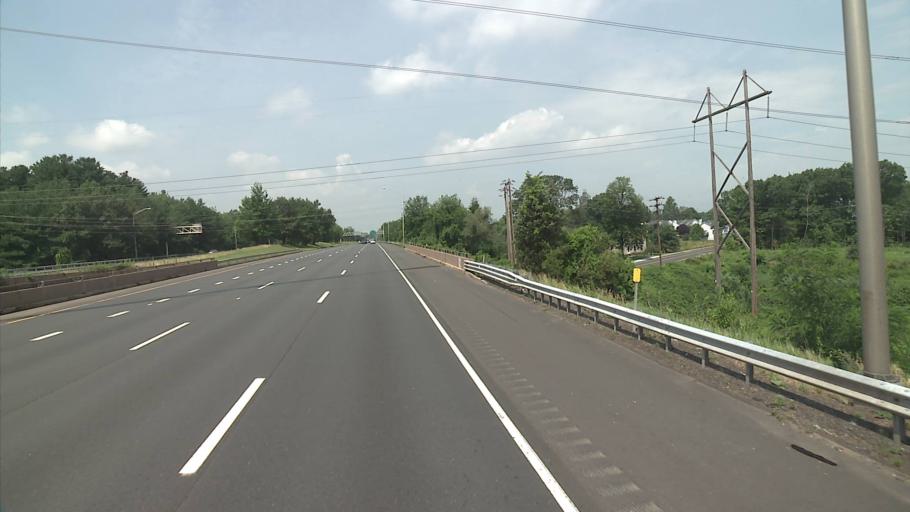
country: US
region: Connecticut
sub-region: Hartford County
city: Manchester
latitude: 41.7650
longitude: -72.5548
